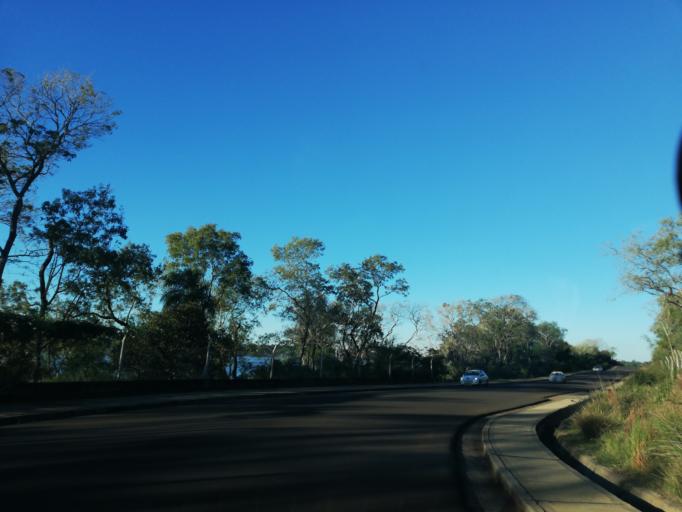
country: AR
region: Misiones
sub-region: Departamento de Candelaria
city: Candelaria
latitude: -27.4500
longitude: -55.7717
